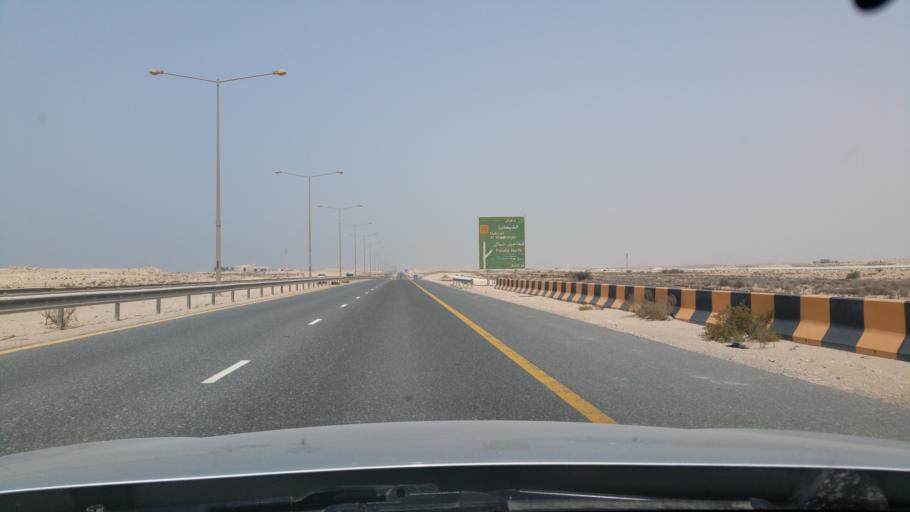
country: QA
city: Umm Bab
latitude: 25.3159
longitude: 50.7908
